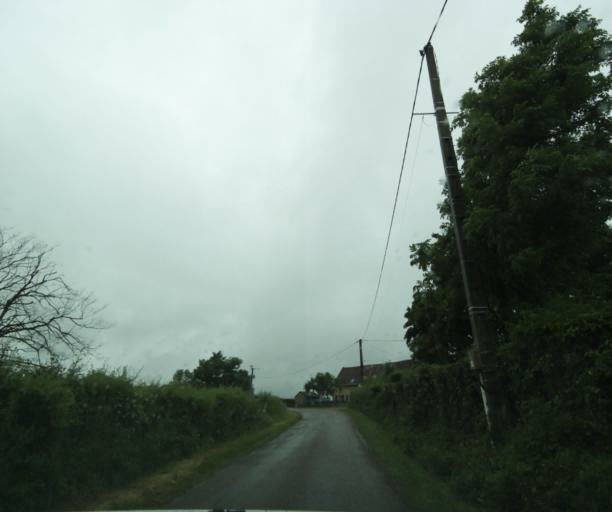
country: FR
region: Bourgogne
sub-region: Departement de Saone-et-Loire
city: Charolles
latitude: 46.4240
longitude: 4.2992
